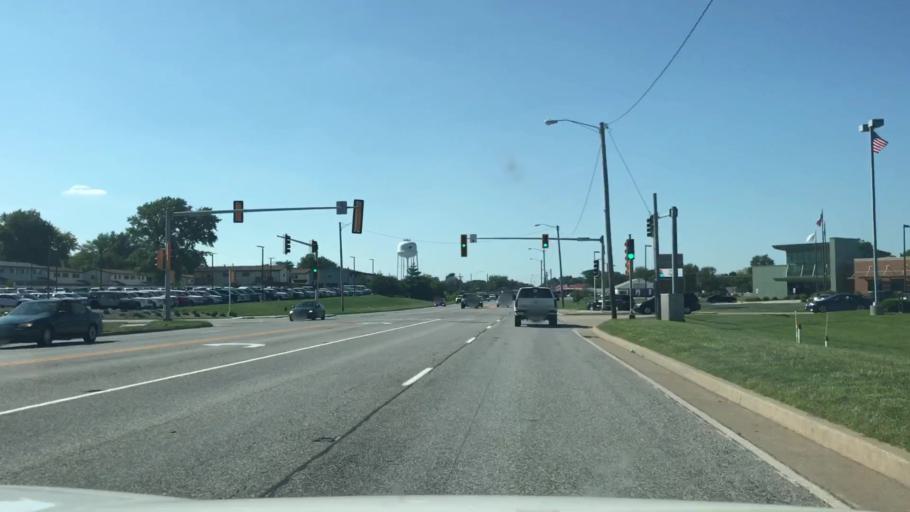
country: US
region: Illinois
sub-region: Madison County
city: Roxana
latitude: 38.8581
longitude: -90.0675
